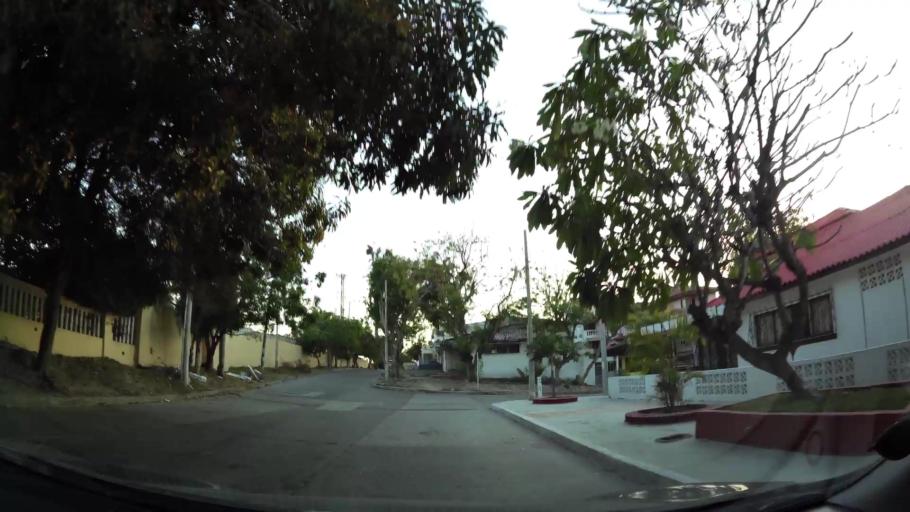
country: CO
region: Atlantico
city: Barranquilla
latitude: 10.9812
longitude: -74.8019
